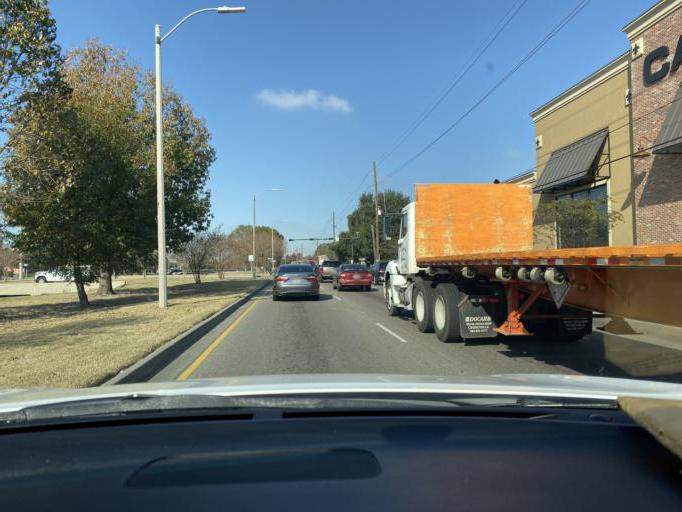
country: US
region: Louisiana
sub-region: Jefferson Parish
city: Terrytown
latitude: 29.9240
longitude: -90.0190
